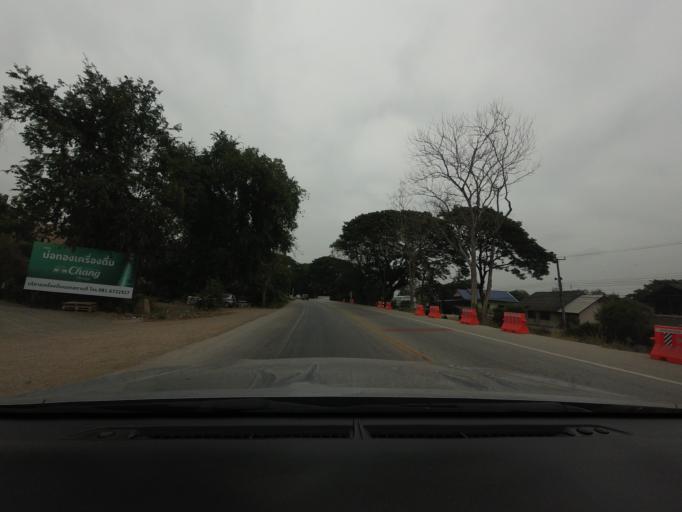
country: TH
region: Lamphun
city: Lamphun
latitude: 18.6111
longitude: 99.0287
